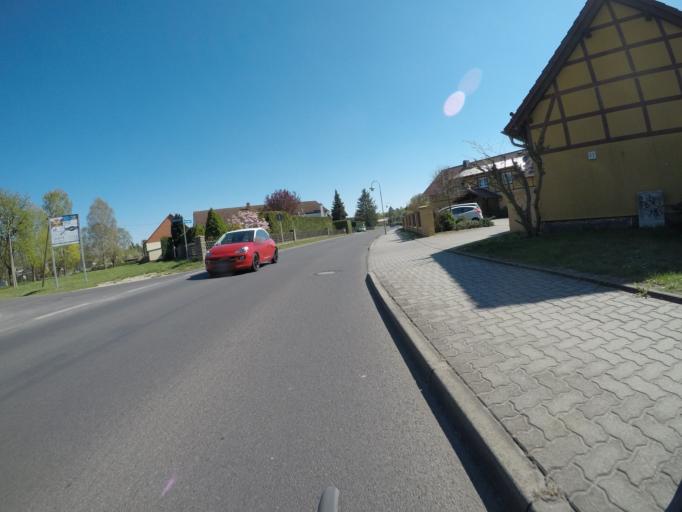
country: DE
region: Brandenburg
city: Strausberg
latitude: 52.6078
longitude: 13.8700
